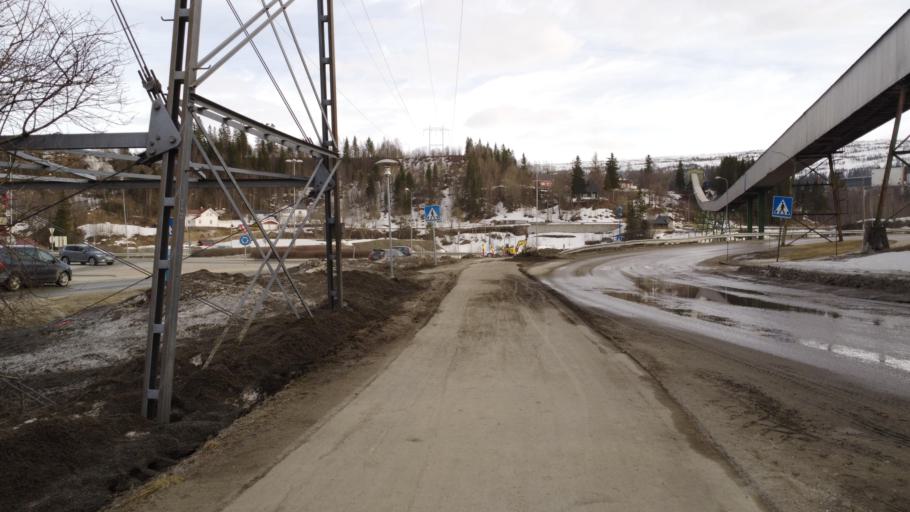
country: NO
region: Nordland
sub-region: Rana
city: Mo i Rana
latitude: 66.3207
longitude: 14.1701
